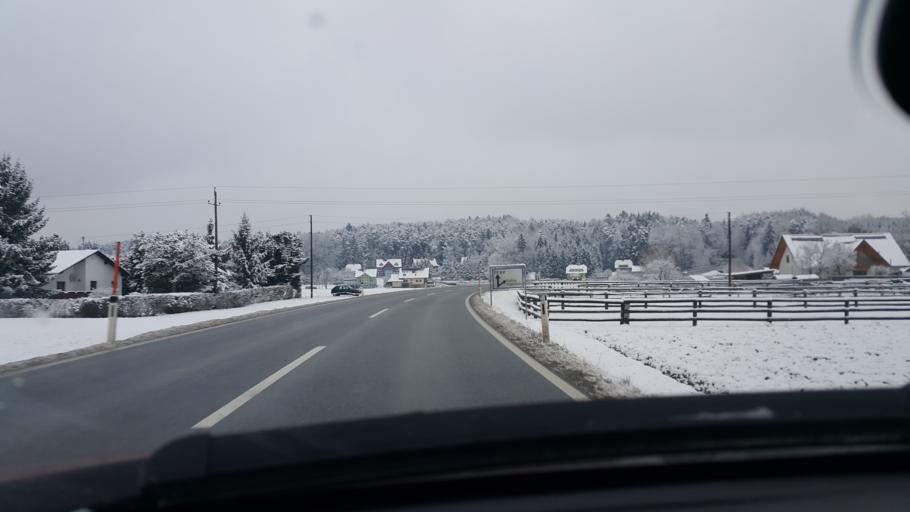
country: AT
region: Styria
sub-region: Politischer Bezirk Graz-Umgebung
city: Hitzendorf
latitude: 47.0137
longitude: 15.2773
